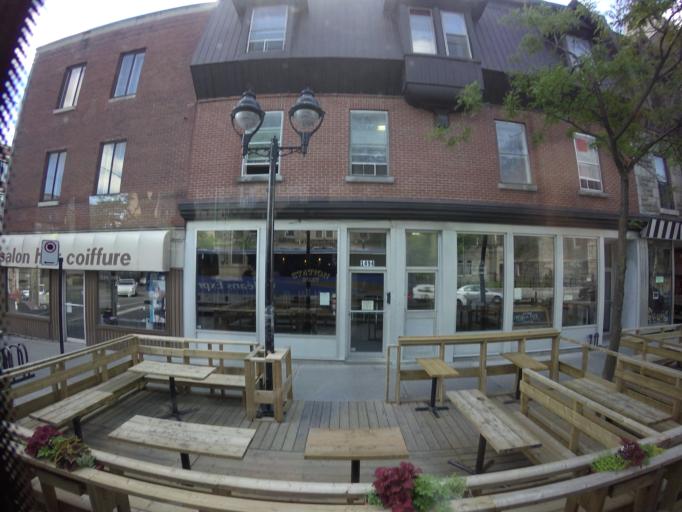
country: CA
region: Quebec
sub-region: Montreal
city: Montreal
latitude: 45.5241
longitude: -73.5605
